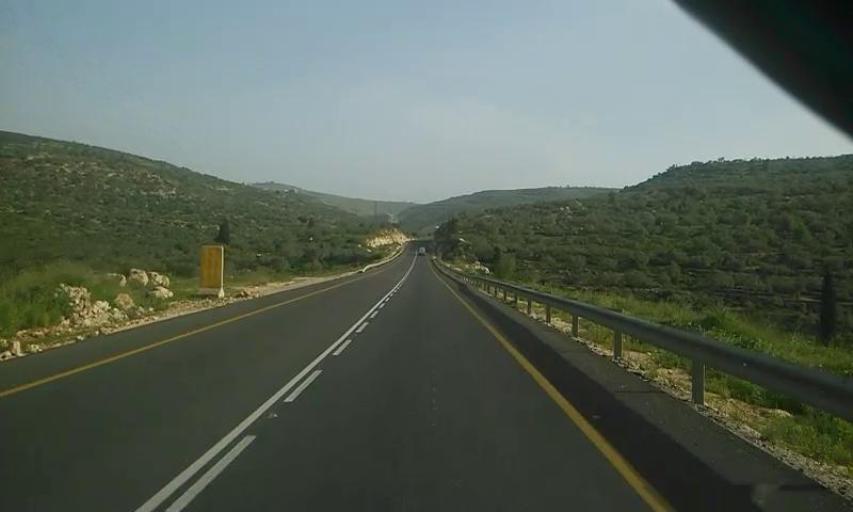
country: PS
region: West Bank
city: Jit
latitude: 32.2239
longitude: 35.1739
